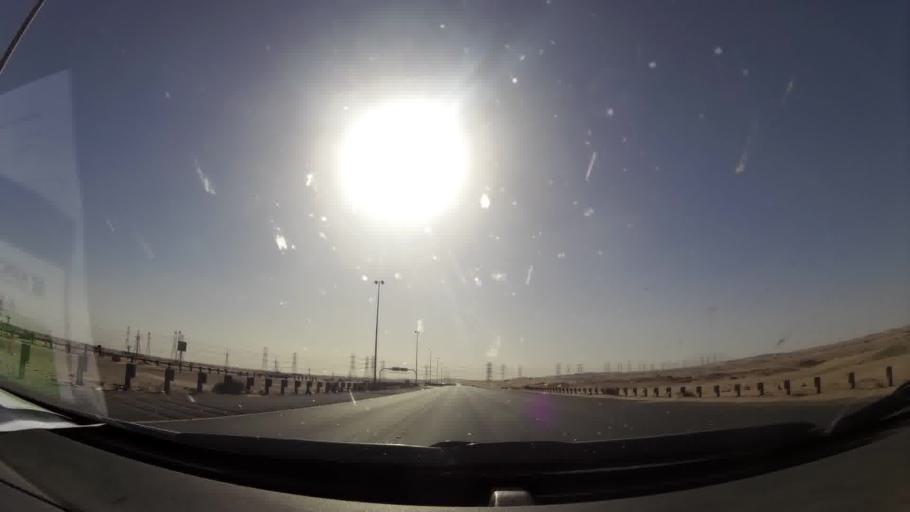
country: KW
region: Al Asimah
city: Kuwait City
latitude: 29.6334
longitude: 47.9317
